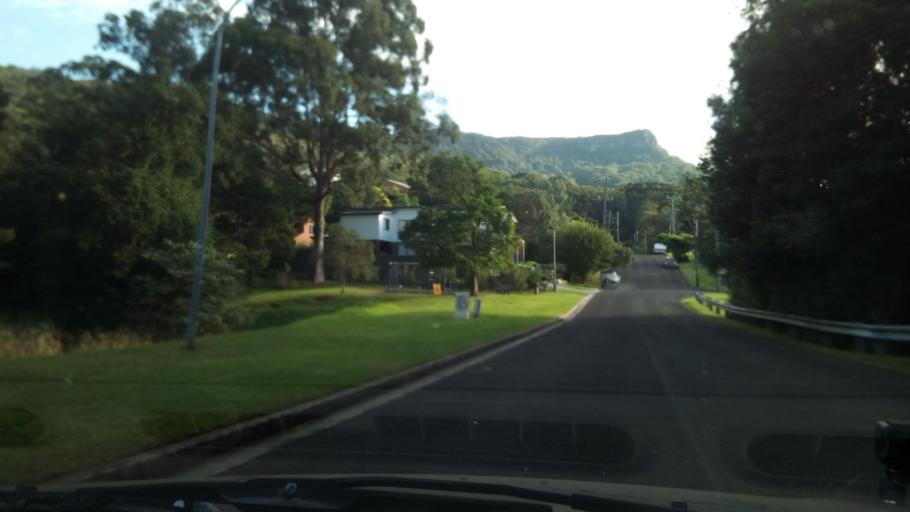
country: AU
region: New South Wales
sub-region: Wollongong
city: Mount Ousley
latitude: -34.3836
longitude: 150.8721
